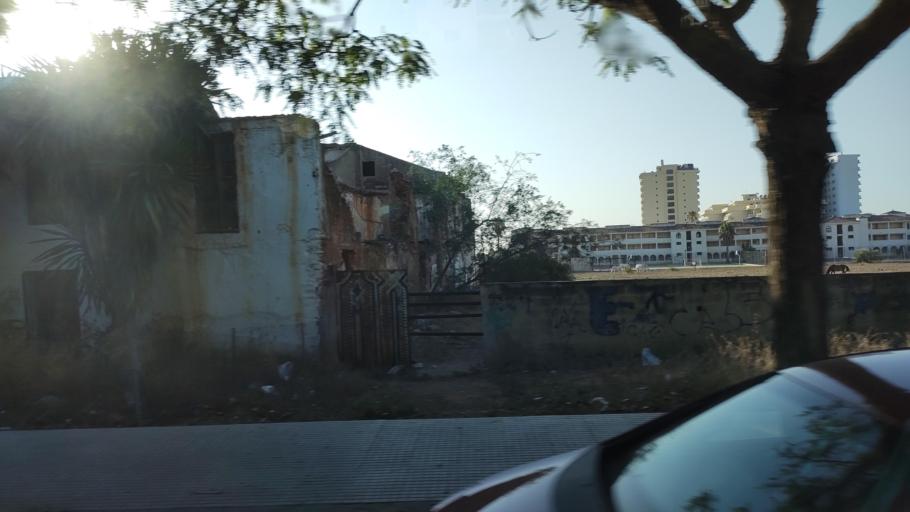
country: ES
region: Andalusia
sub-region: Provincia de Malaga
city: Torremolinos
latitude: 36.6395
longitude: -4.4880
